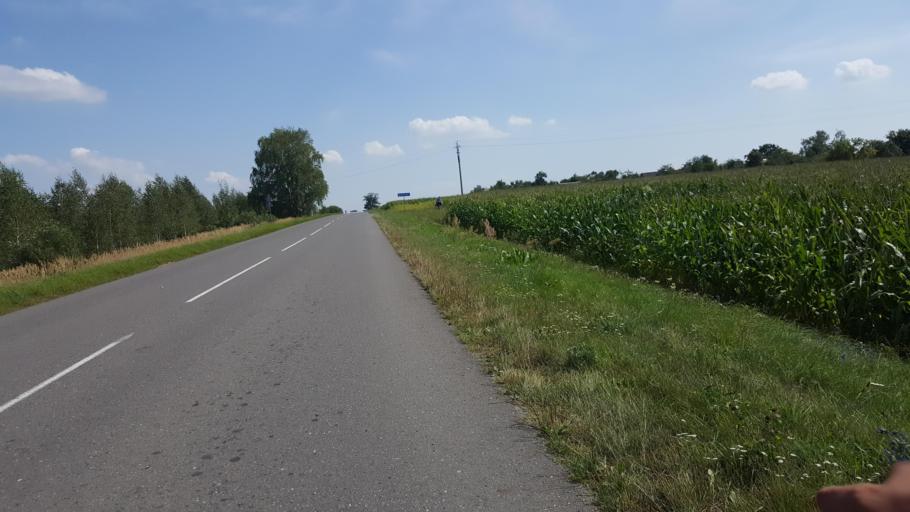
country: BY
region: Brest
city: Kamyanyuki
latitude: 52.5028
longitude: 23.6631
